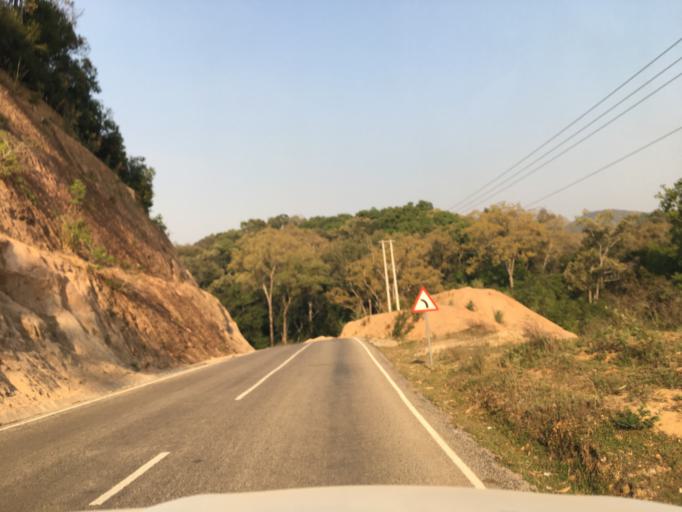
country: LA
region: Houaphan
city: Xam Nua
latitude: 20.5912
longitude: 104.0653
